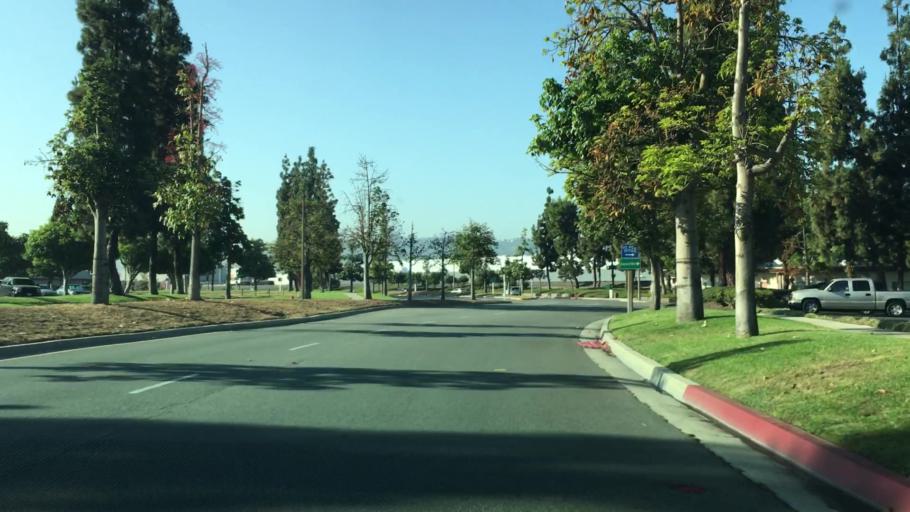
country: US
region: California
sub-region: Los Angeles County
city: La Puente
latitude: 34.0220
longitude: -117.9551
